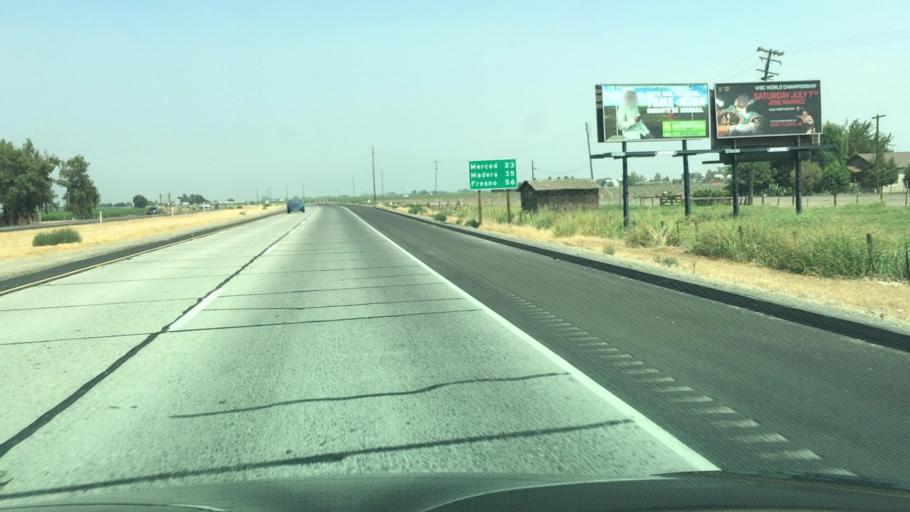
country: US
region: California
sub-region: Merced County
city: Dos Palos
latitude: 37.0485
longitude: -120.6263
